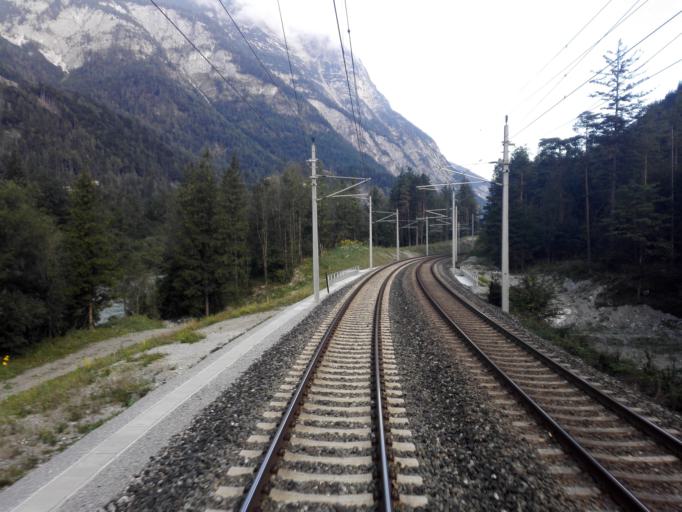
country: AT
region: Salzburg
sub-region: Politischer Bezirk Sankt Johann im Pongau
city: Werfen
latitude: 47.5154
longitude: 13.1671
